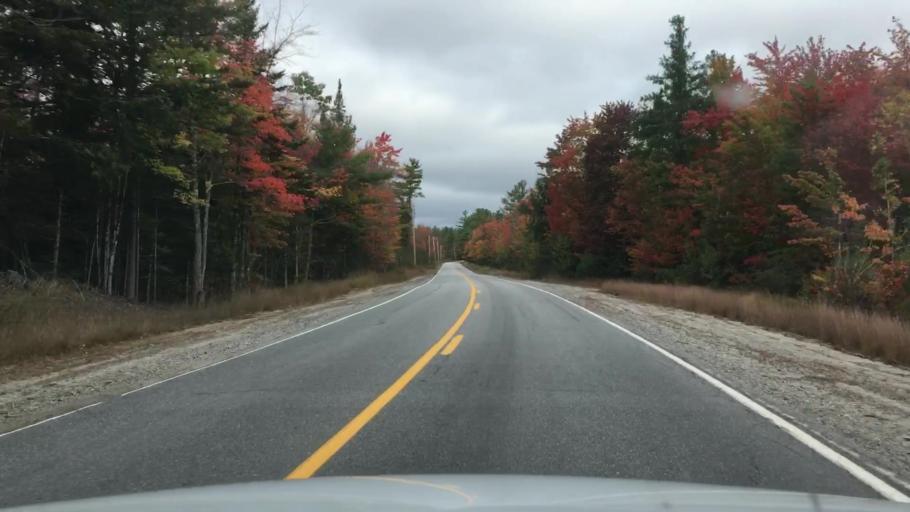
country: US
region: Maine
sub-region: Oxford County
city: Bethel
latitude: 44.3253
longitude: -70.7704
